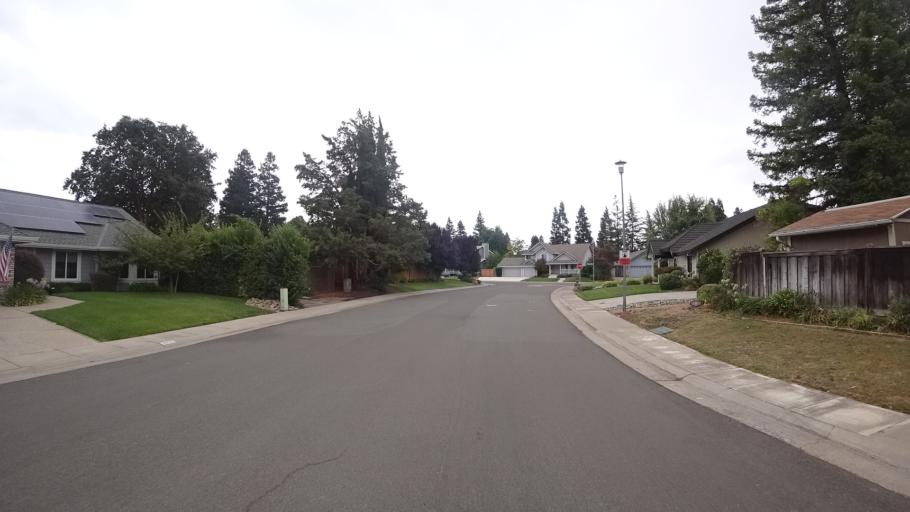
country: US
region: California
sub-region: Sacramento County
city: Laguna
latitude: 38.4198
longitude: -121.4441
